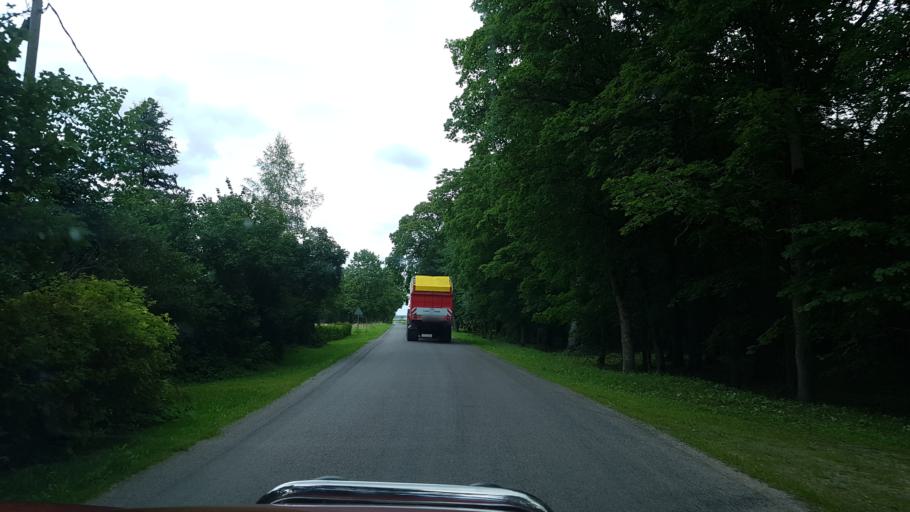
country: EE
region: Laeaene
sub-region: Lihula vald
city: Lihula
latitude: 58.7074
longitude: 24.0276
